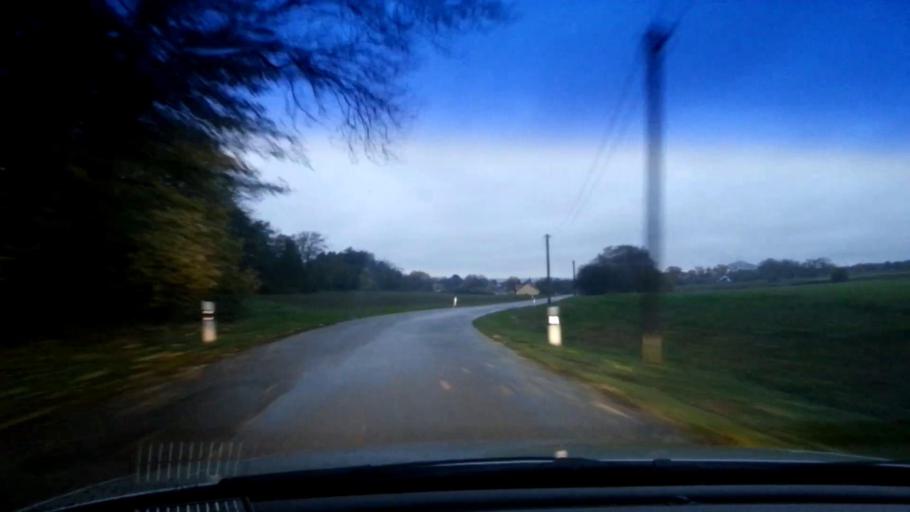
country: DE
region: Bavaria
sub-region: Upper Franconia
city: Schesslitz
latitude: 49.9471
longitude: 11.0426
